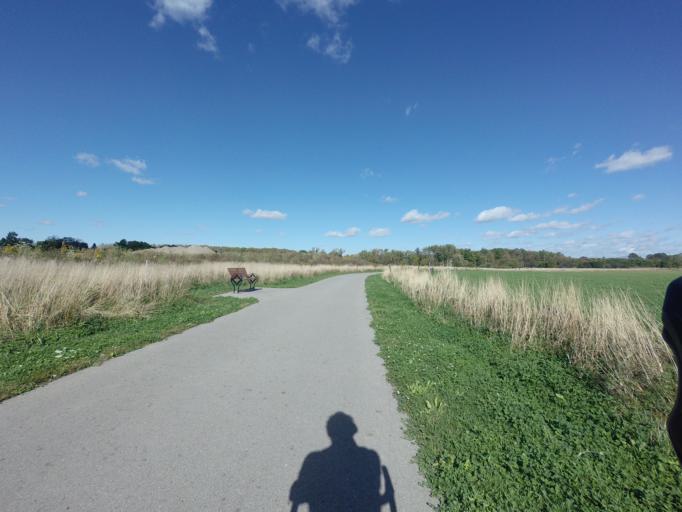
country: CA
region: Ontario
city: Ajax
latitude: 43.8501
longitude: -78.9715
